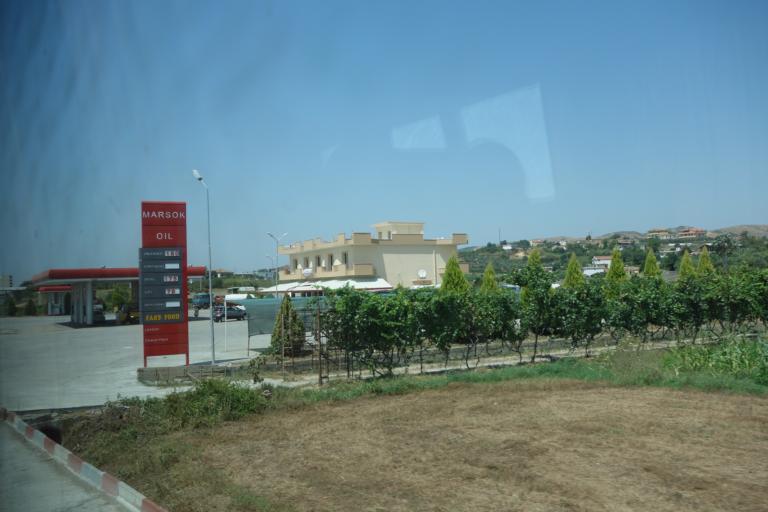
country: AL
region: Tirane
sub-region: Rrethi i Kavajes
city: Gose e Madhe
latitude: 41.0832
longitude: 19.6198
